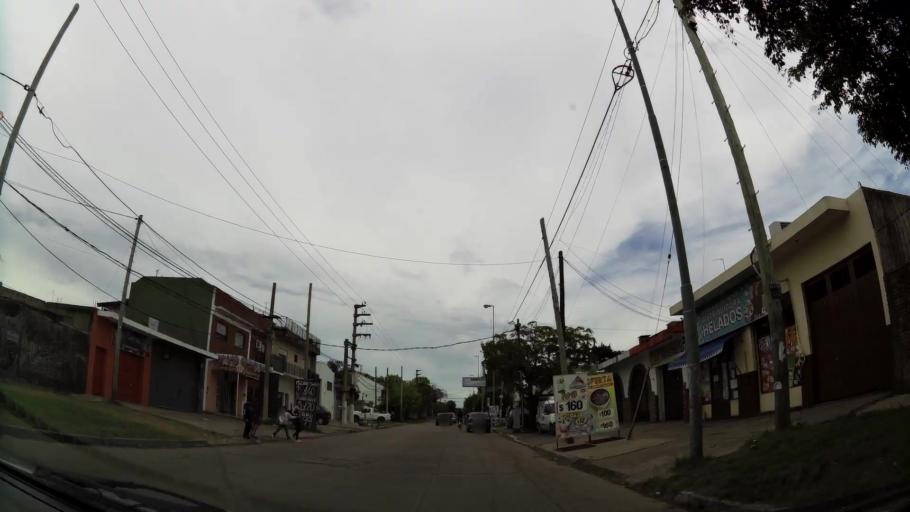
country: AR
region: Buenos Aires
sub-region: Partido de Quilmes
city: Quilmes
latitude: -34.7557
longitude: -58.2335
